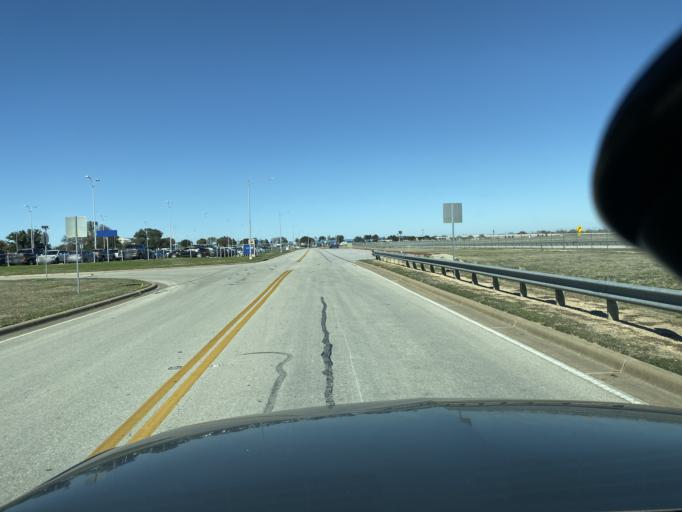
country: US
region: Texas
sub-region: Travis County
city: Hornsby Bend
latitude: 30.2048
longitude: -97.6609
